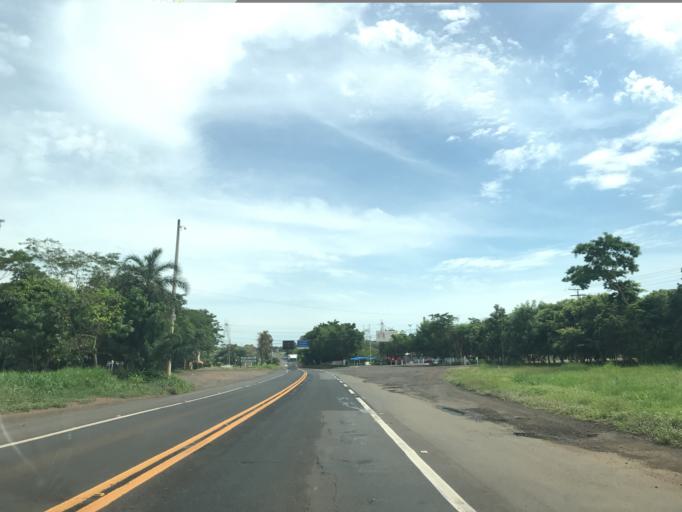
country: BR
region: Sao Paulo
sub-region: Nova Granada
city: Nova Granada
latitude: -20.3091
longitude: -49.2083
